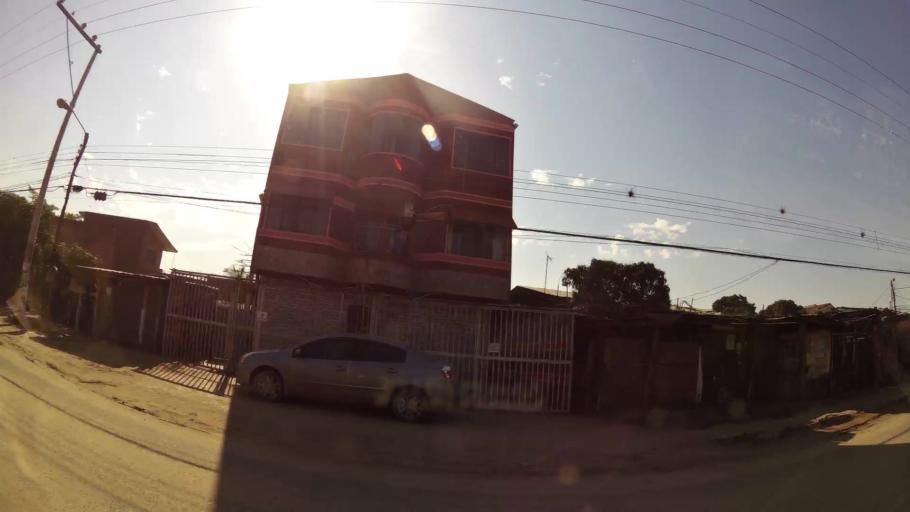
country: BO
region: Santa Cruz
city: Santa Cruz de la Sierra
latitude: -17.8281
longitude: -63.1379
